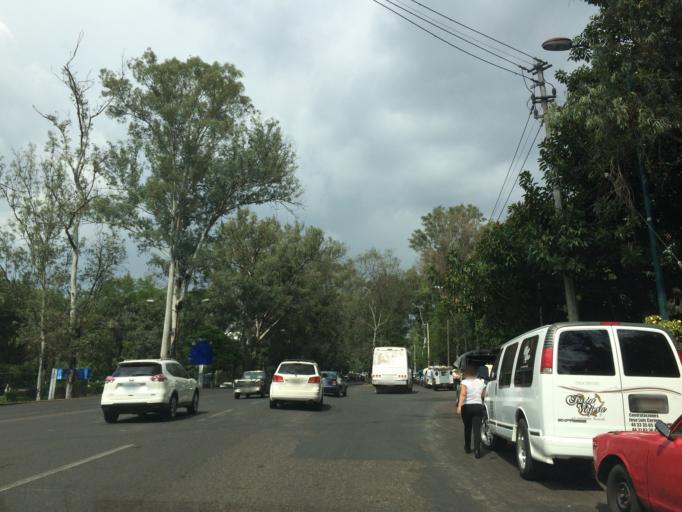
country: MX
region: Michoacan
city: Morelia
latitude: 19.6817
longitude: -101.1949
